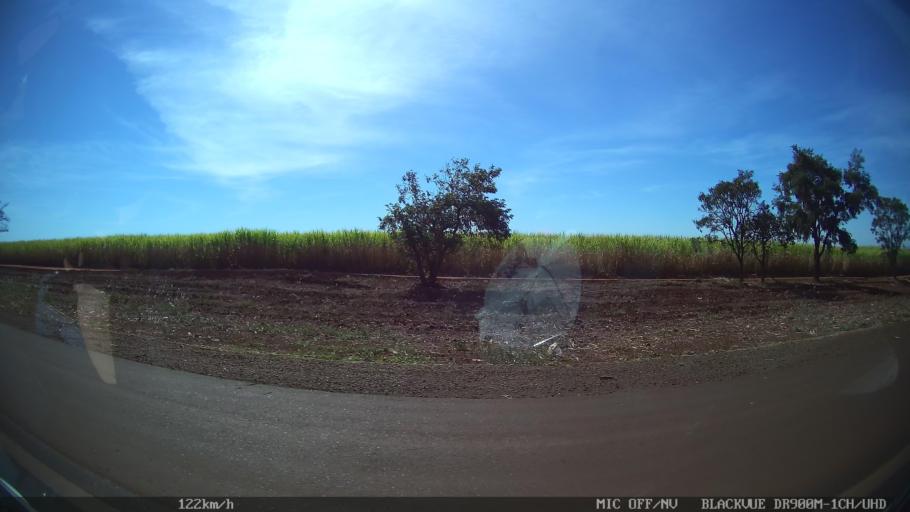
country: BR
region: Sao Paulo
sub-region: Ipua
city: Ipua
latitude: -20.4995
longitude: -47.9574
